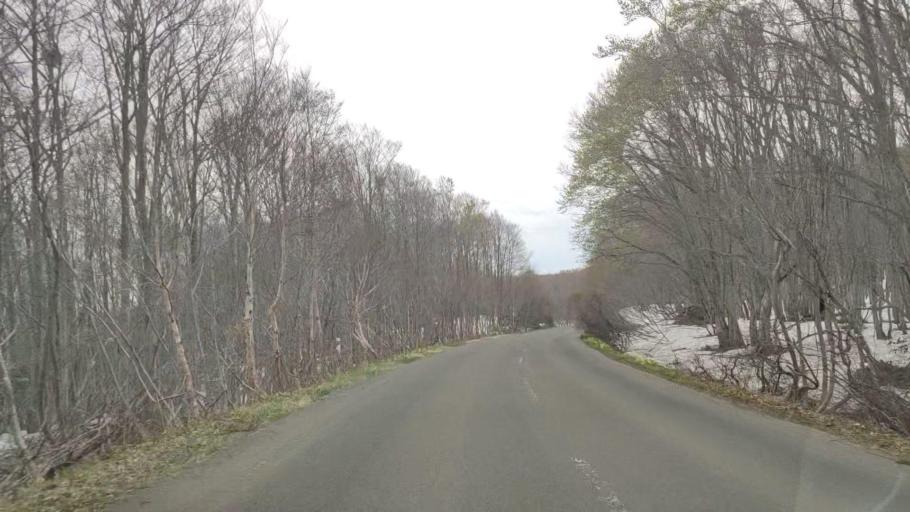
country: JP
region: Aomori
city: Aomori Shi
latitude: 40.6895
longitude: 140.9170
